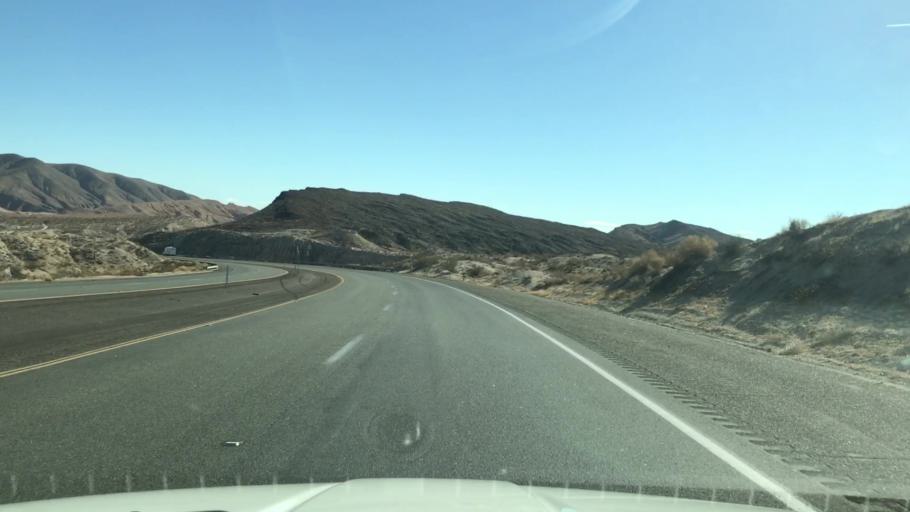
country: US
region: California
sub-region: Kern County
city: California City
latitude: 35.3854
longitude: -117.9847
